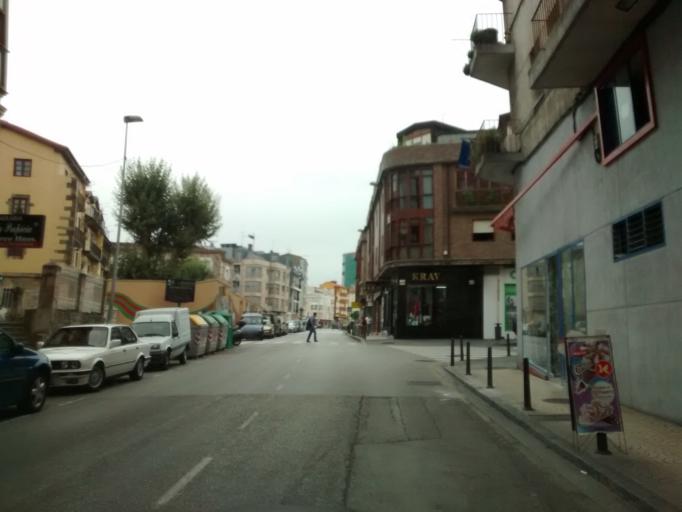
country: ES
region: Cantabria
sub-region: Provincia de Cantabria
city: Torrelavega
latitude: 43.3478
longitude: -4.0497
